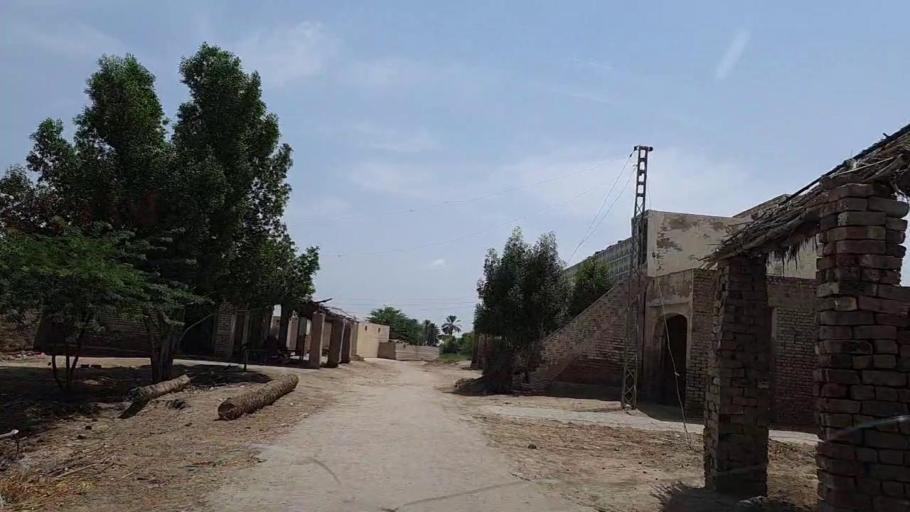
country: PK
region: Sindh
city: Khanpur
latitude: 27.7917
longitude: 69.4563
